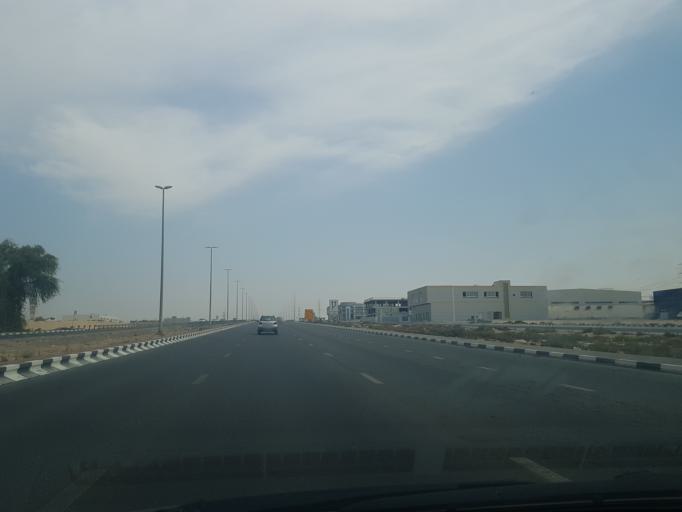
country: AE
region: Ash Shariqah
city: Sharjah
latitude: 25.2467
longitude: 55.5442
